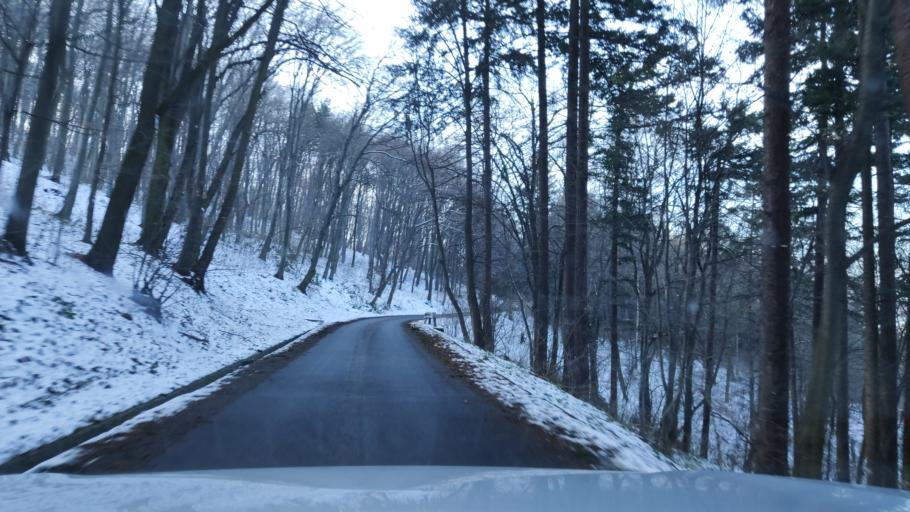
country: RS
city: Rusanj
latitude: 44.6992
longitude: 20.5179
